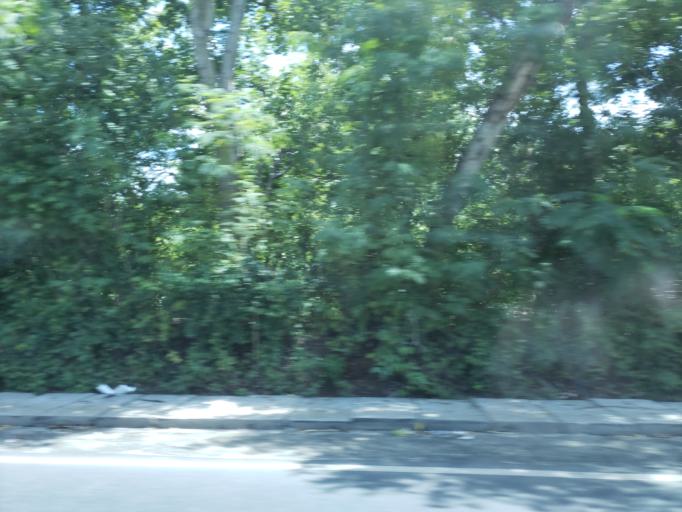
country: ID
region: Bali
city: Jimbaran
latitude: -8.7893
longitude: 115.1642
